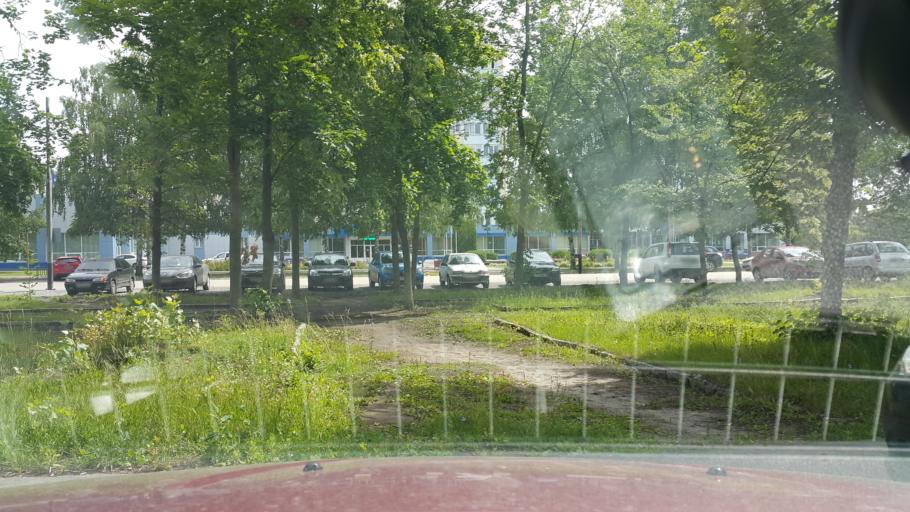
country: RU
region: Tambov
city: Donskoye
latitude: 52.7429
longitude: 41.4814
